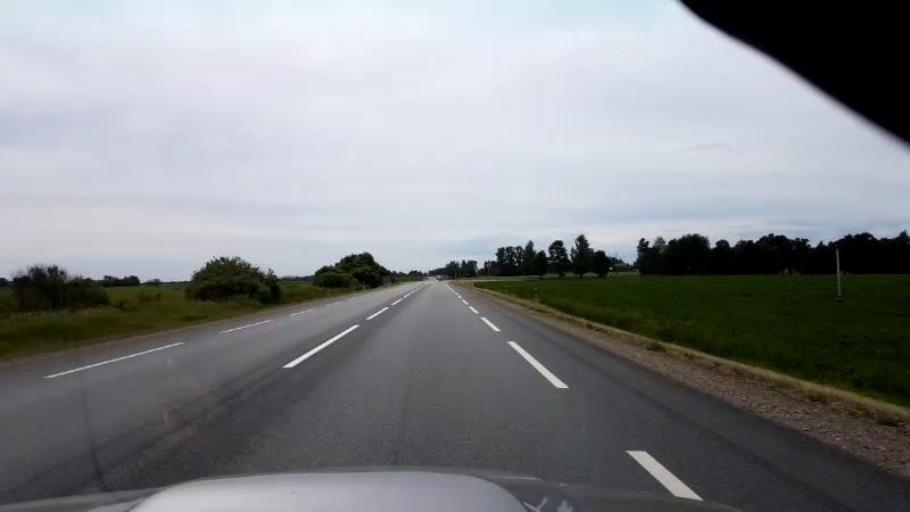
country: LV
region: Lecava
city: Iecava
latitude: 56.5694
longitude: 24.1754
